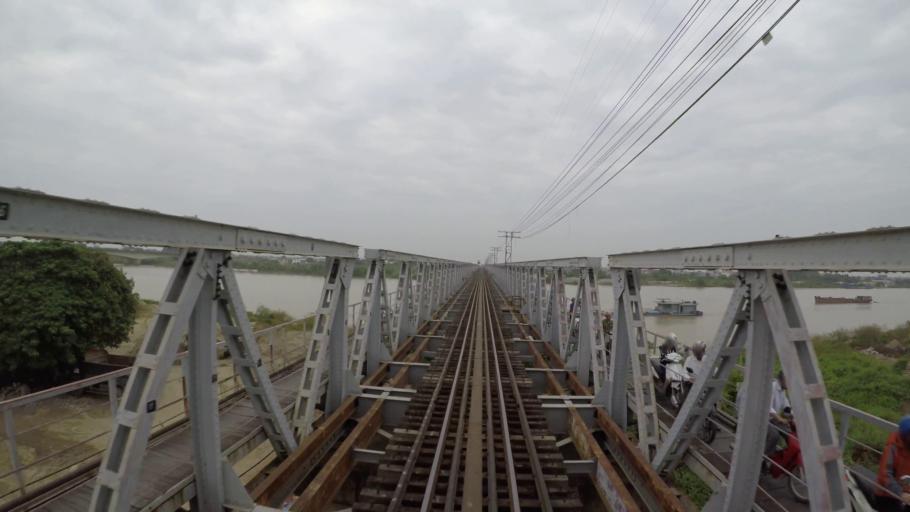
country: VN
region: Hai Duong
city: Thanh Pho Hai Duong
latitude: 20.9548
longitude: 106.3637
